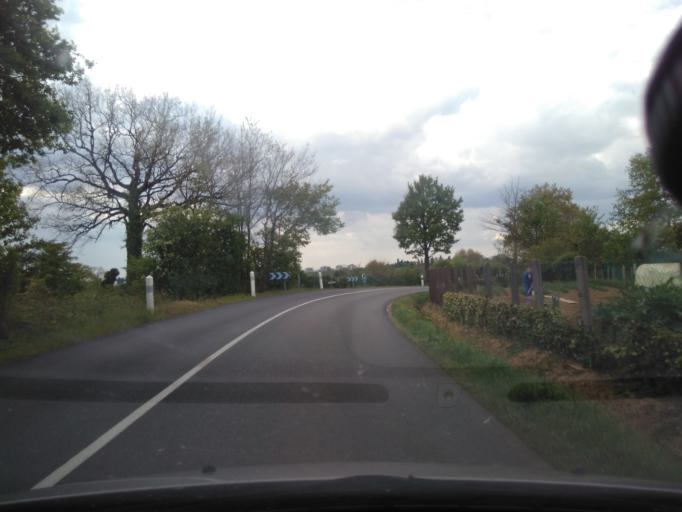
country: FR
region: Pays de la Loire
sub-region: Departement de la Vendee
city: La Roche-sur-Yon
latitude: 46.6989
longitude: -1.4207
